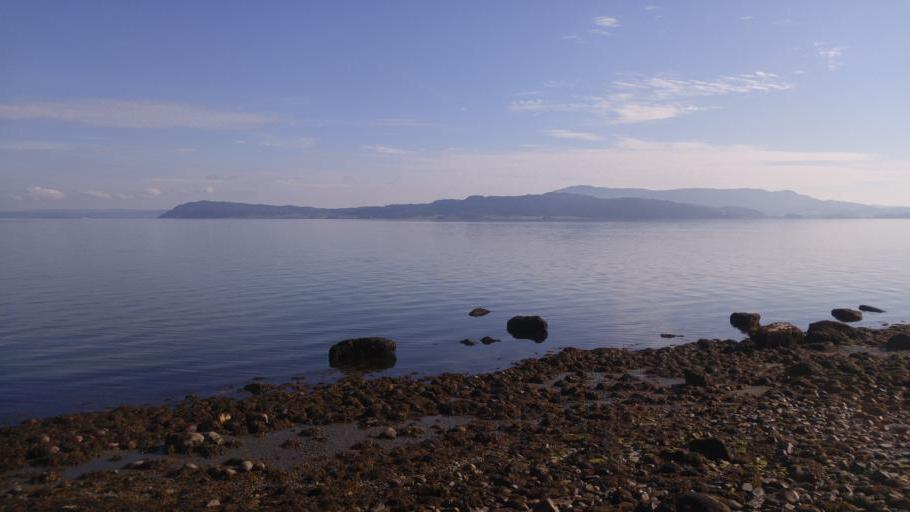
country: NO
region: Sor-Trondelag
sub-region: Malvik
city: Hommelvik
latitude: 63.4320
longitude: 10.7595
